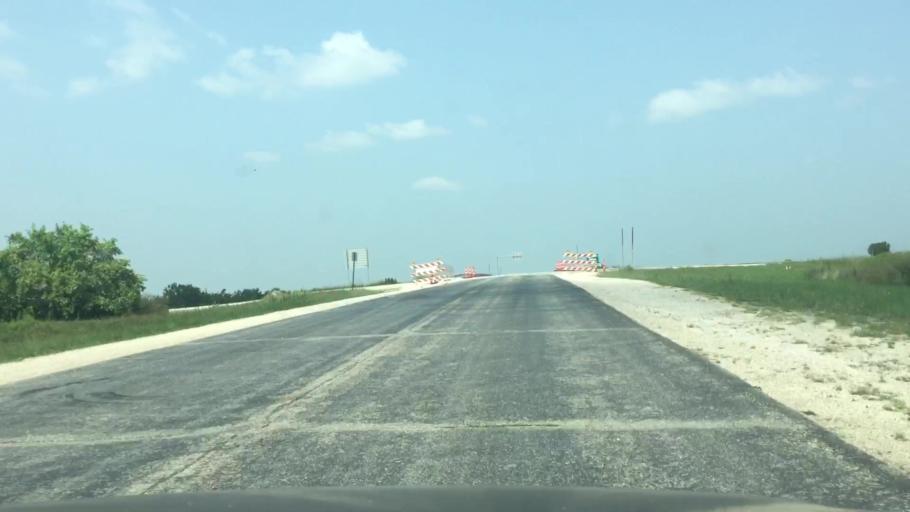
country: US
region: Kansas
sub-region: Allen County
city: Iola
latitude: 37.8796
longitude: -95.3948
